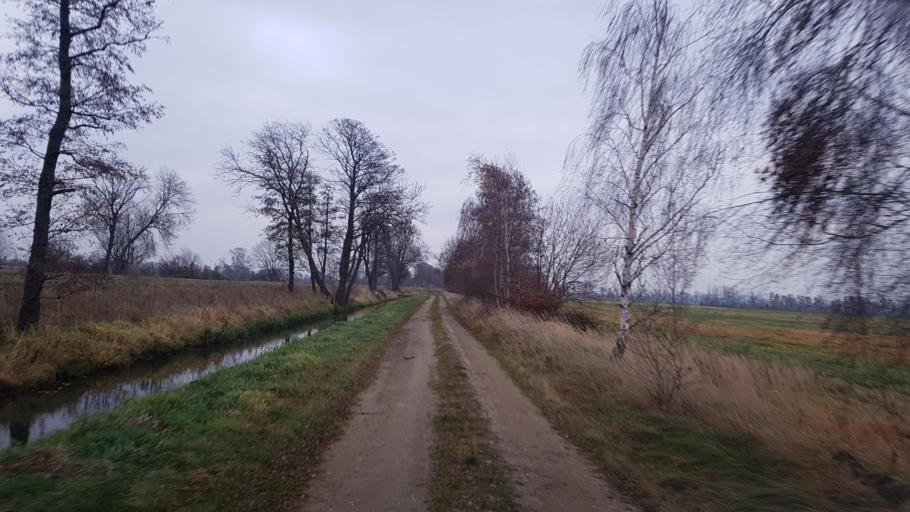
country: DE
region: Brandenburg
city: Hirschfeld
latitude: 51.4155
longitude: 13.6039
